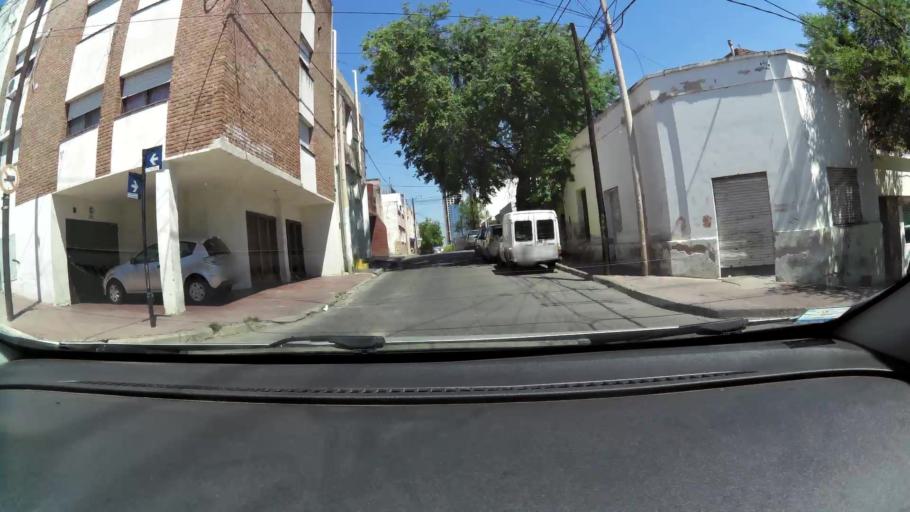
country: AR
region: Cordoba
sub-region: Departamento de Capital
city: Cordoba
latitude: -31.4013
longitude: -64.1936
